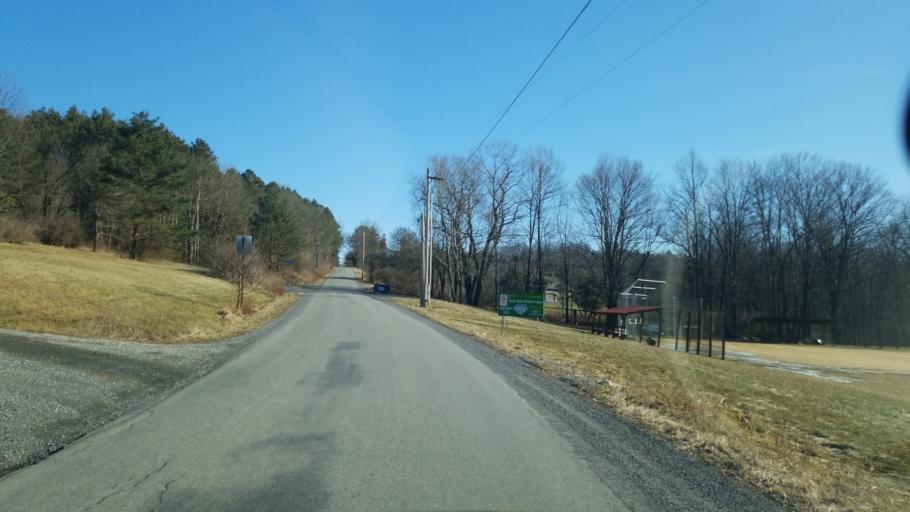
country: US
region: Pennsylvania
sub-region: Jefferson County
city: Sykesville
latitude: 41.0505
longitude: -78.7919
